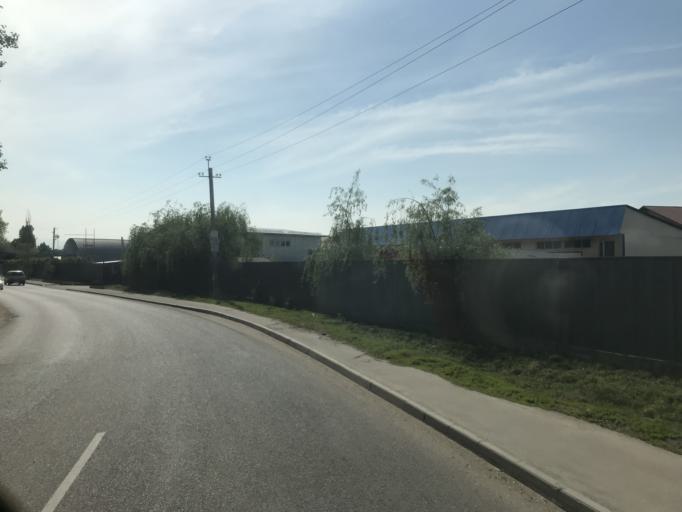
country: KZ
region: Almaty Qalasy
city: Almaty
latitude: 43.2397
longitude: 76.8056
